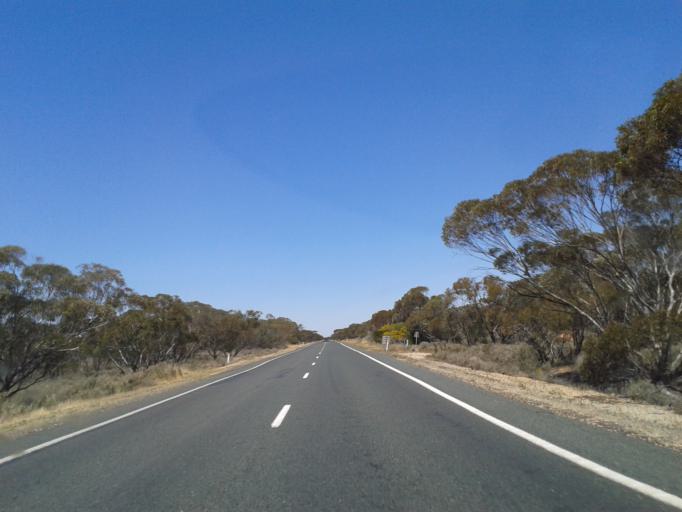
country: AU
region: New South Wales
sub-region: Wentworth
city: Gol Gol
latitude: -34.5203
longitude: 142.6150
